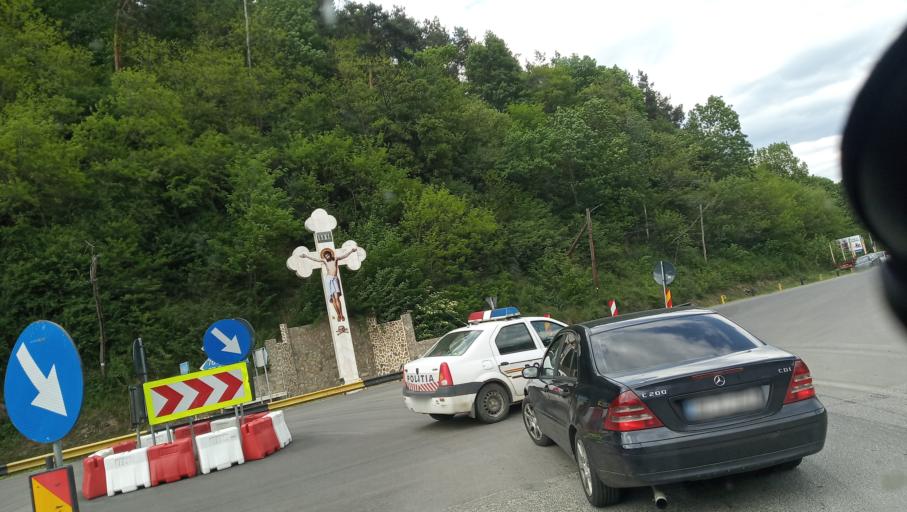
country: RO
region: Alba
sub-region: Oras Campeni
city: Campeni
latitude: 46.3605
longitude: 23.0771
